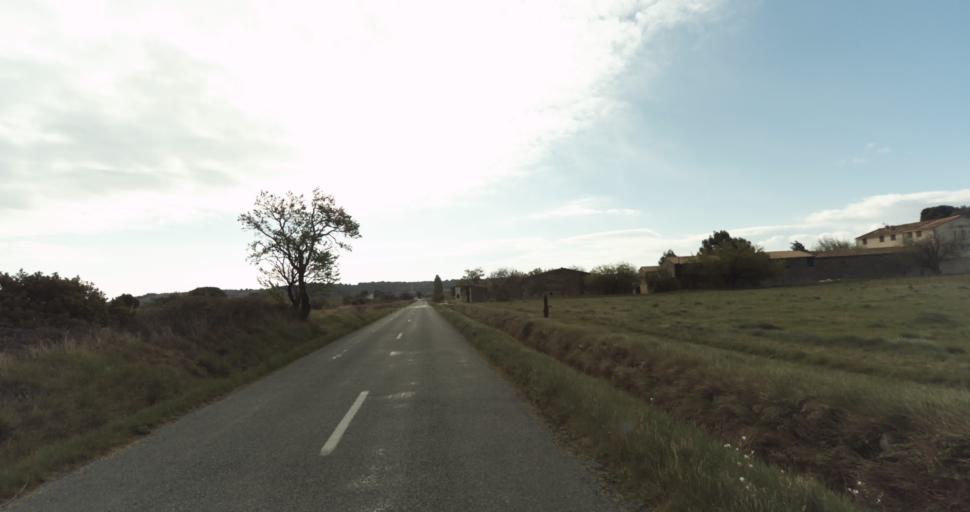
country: FR
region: Languedoc-Roussillon
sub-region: Departement de l'Aude
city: Leucate
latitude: 42.9309
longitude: 3.0001
